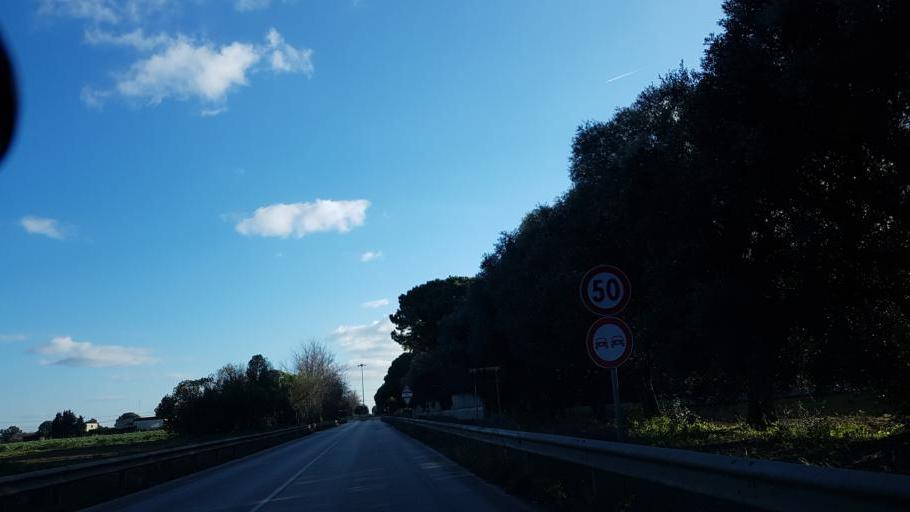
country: IT
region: Apulia
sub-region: Provincia di Brindisi
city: La Rosa
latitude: 40.6114
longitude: 17.9531
